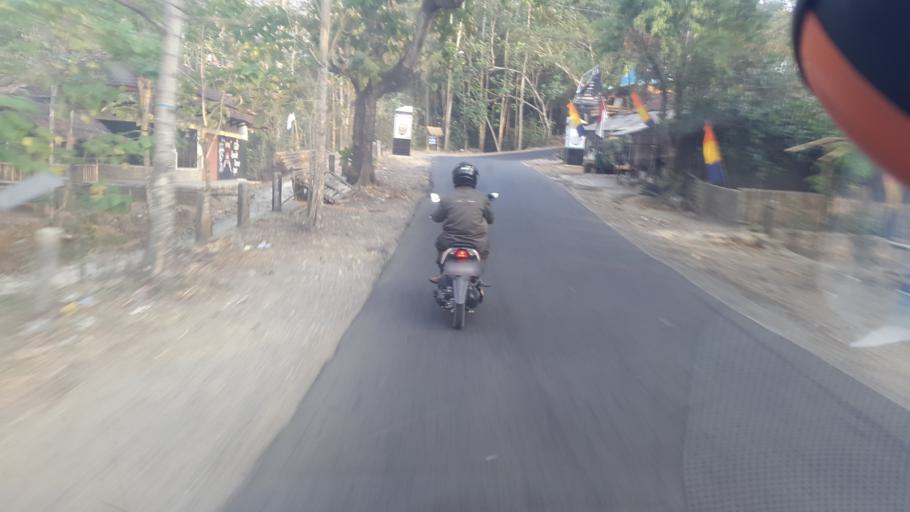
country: ID
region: West Java
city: Pondokaso
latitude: -7.3518
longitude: 106.5336
